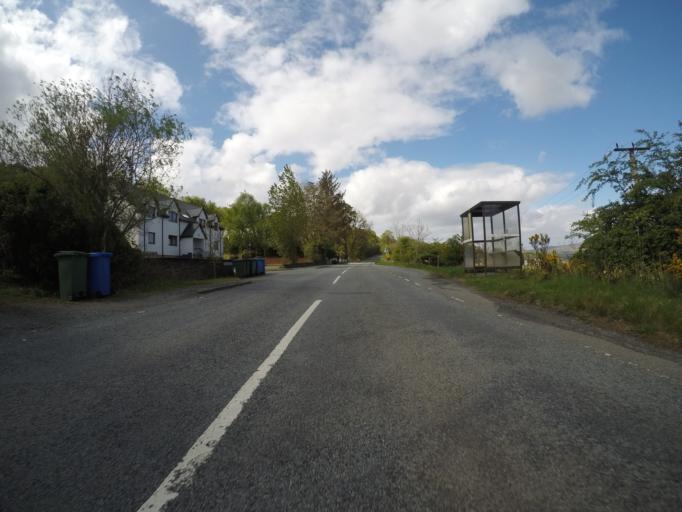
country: GB
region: Scotland
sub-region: Highland
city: Isle of Skye
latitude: 57.4575
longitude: -6.3264
